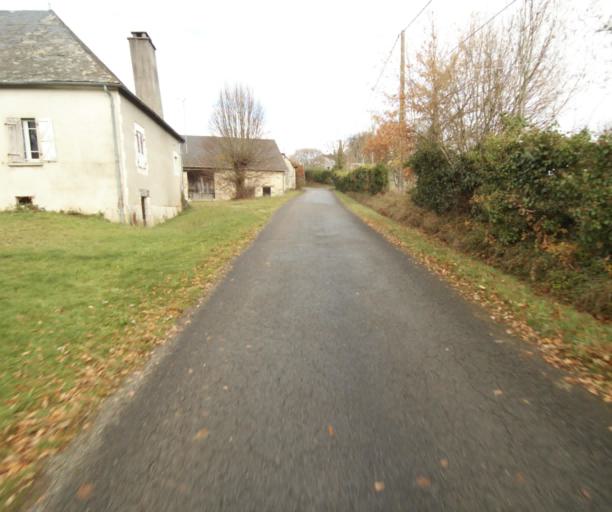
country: FR
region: Limousin
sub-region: Departement de la Correze
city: Sainte-Fereole
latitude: 45.2610
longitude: 1.6034
